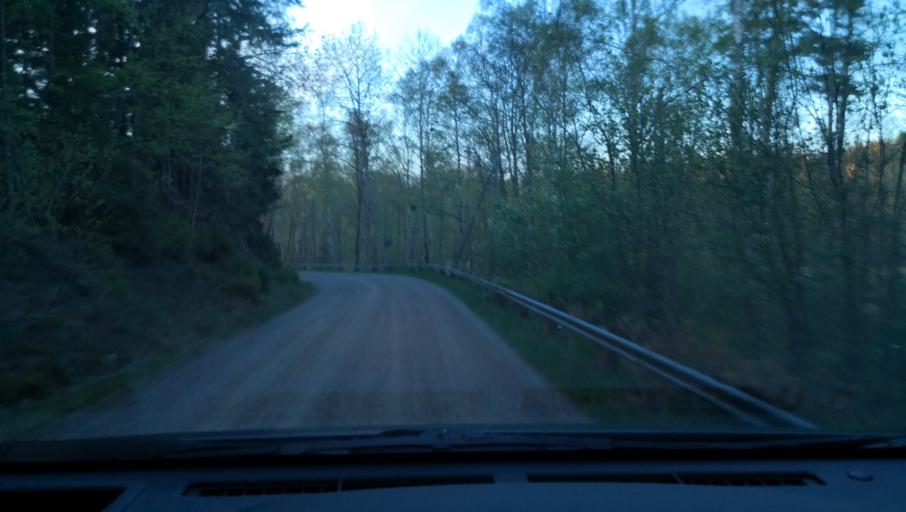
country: SE
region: OErebro
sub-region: Askersunds Kommun
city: Asbro
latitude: 58.9766
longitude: 14.9474
